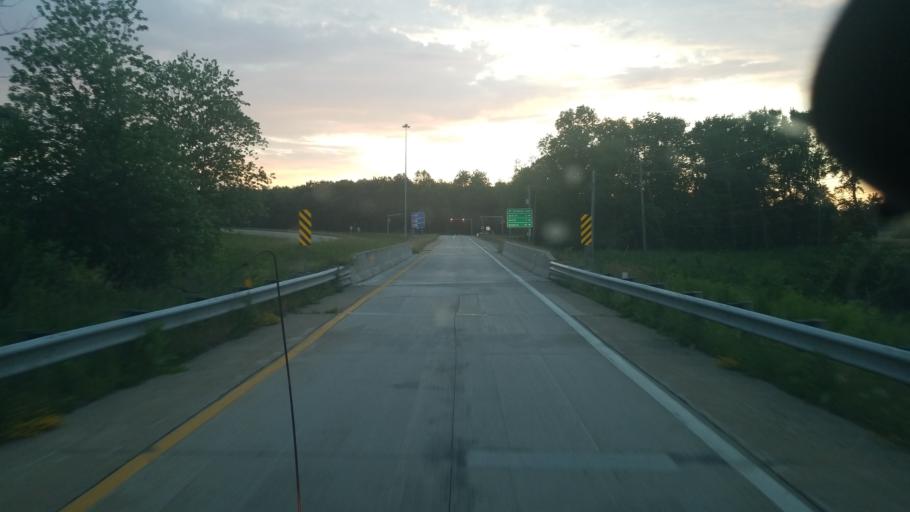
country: US
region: Ohio
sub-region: Licking County
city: Buckeye Lake
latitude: 39.9466
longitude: -82.4779
